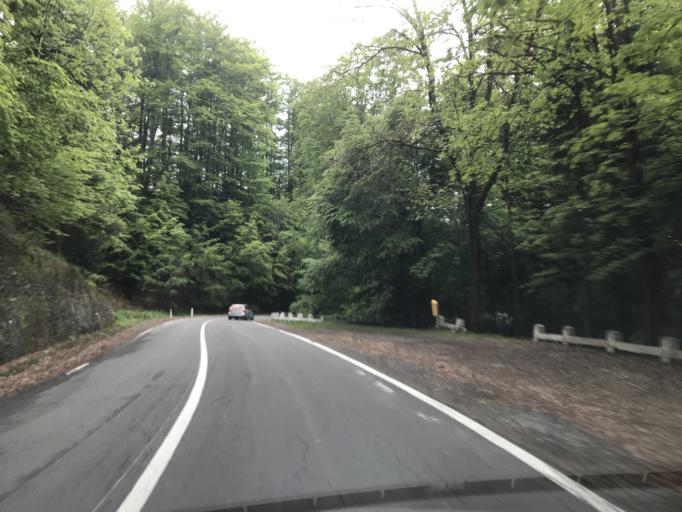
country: RO
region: Sibiu
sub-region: Comuna Cartisoara
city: Cartisoara
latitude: 45.6749
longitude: 24.5836
